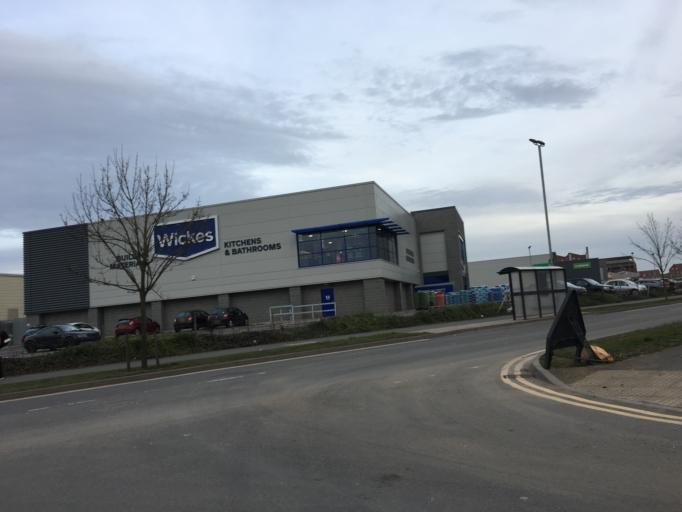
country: GB
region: England
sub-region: Warwickshire
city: Rugby
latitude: 52.3846
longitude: -1.2607
